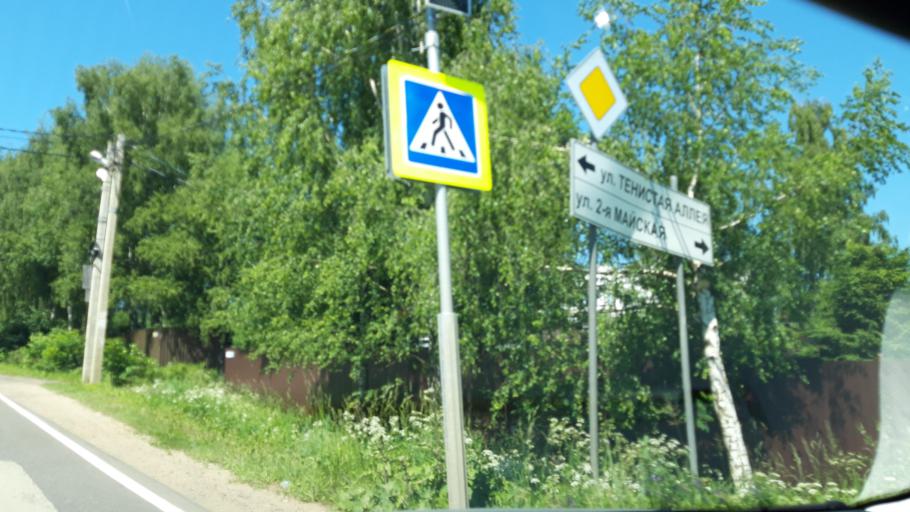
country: RU
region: Moskovskaya
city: Solnechnogorsk
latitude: 56.1664
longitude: 36.9650
